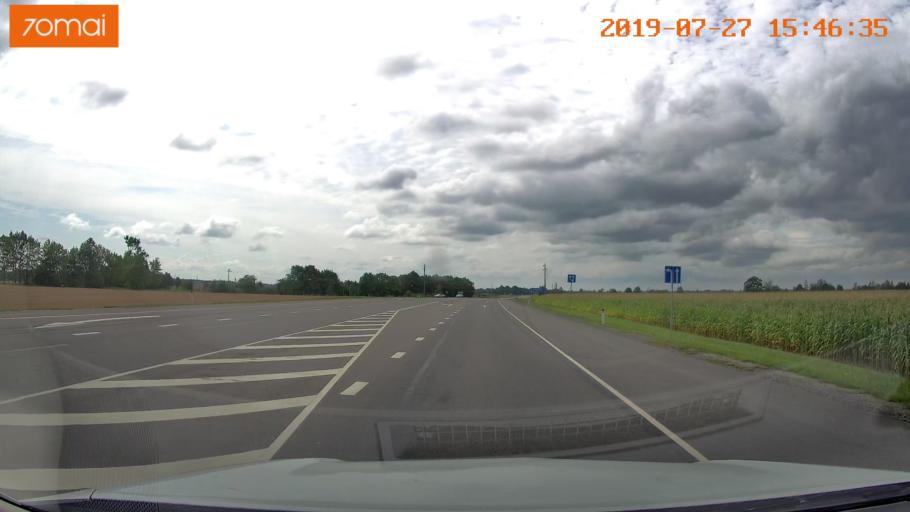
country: RU
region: Kaliningrad
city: Gusev
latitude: 54.6034
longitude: 22.1069
